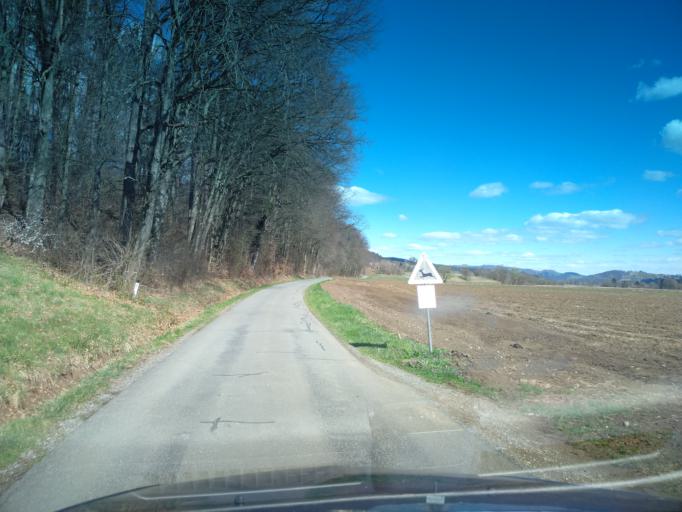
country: AT
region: Styria
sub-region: Politischer Bezirk Leibnitz
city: Sankt Johann im Saggautal
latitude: 46.7104
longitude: 15.3944
